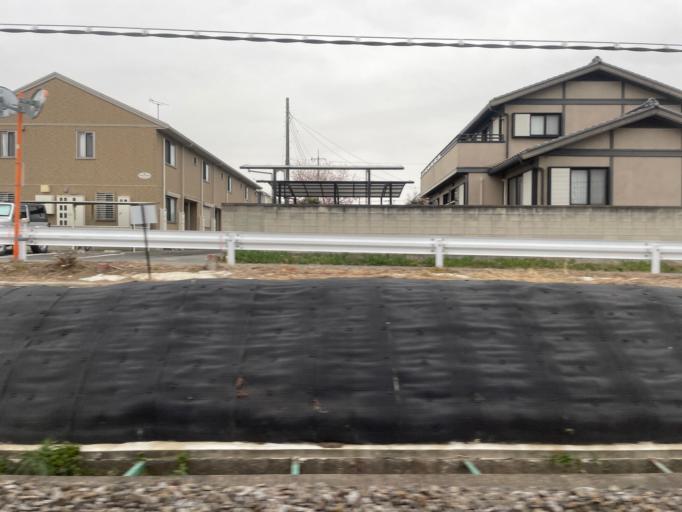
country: JP
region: Gunma
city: Kanekomachi
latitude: 36.4269
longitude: 139.0299
